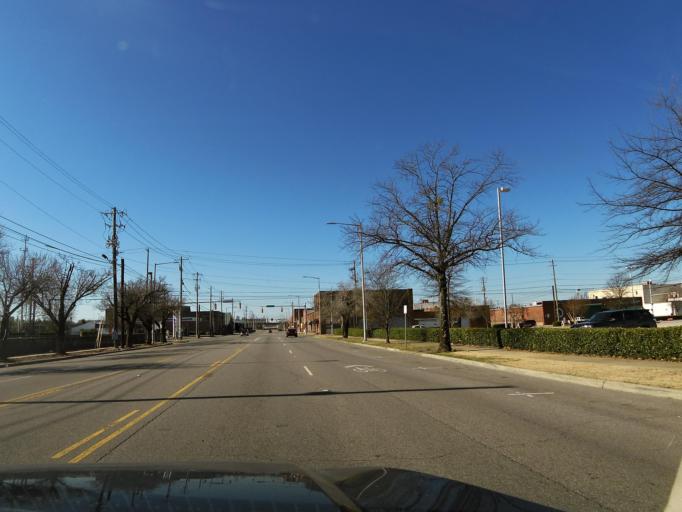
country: US
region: Alabama
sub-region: Jefferson County
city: Birmingham
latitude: 33.5110
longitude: -86.8131
